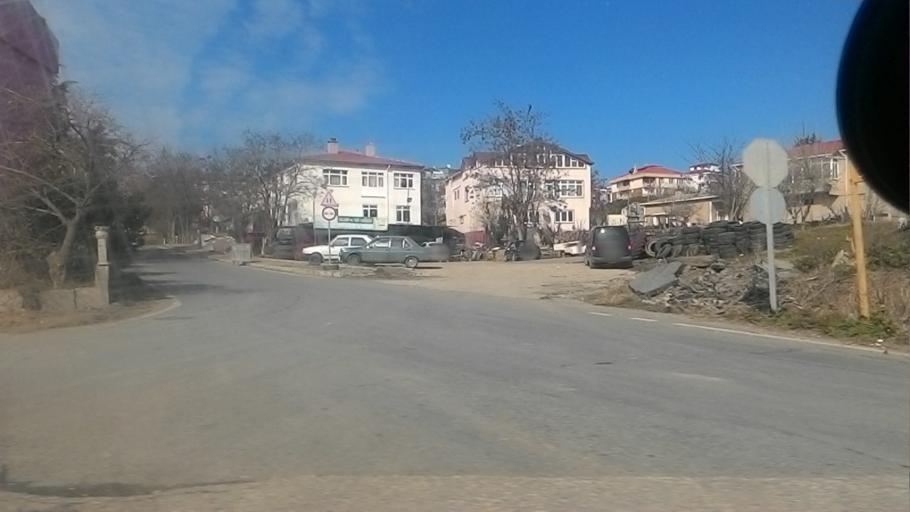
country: TR
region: Istanbul
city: Canta
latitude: 41.0767
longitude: 28.0804
